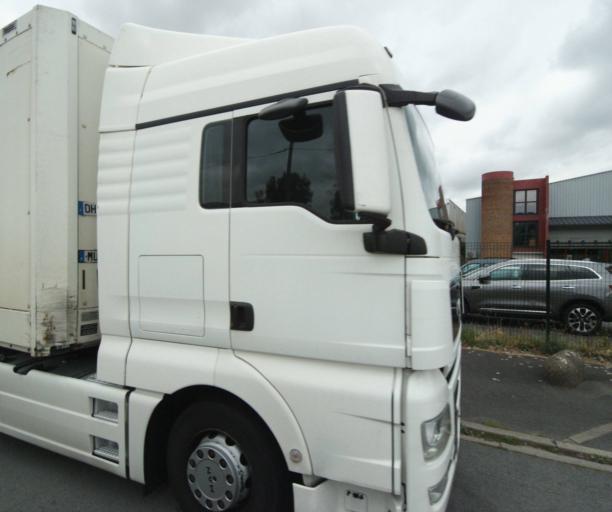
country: FR
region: Nord-Pas-de-Calais
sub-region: Departement du Nord
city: Lesquin
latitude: 50.5832
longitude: 3.1169
